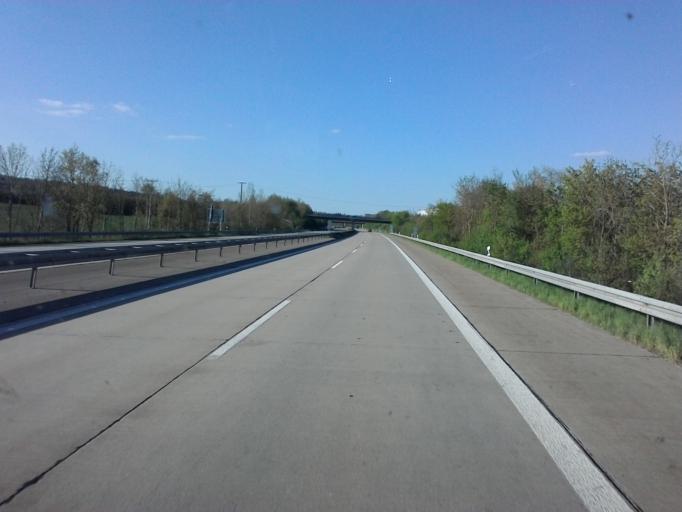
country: DE
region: Bavaria
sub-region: Regierungsbezirk Mittelfranken
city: Schillingsfurst
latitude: 49.2558
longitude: 10.2291
